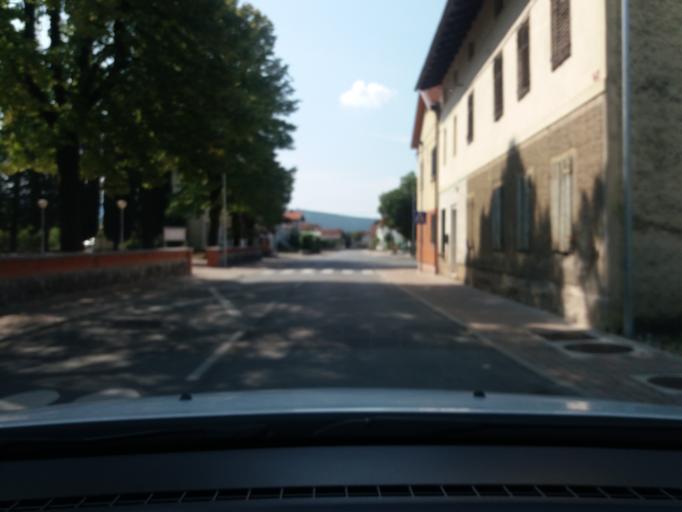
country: SI
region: Sempeter-Vrtojba
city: Vrtojba
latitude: 45.9119
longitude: 13.6351
